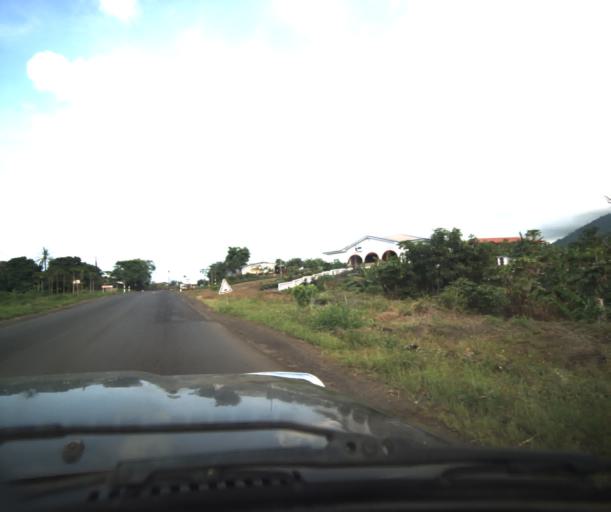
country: CM
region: South-West Province
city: Limbe
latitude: 4.0132
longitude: 9.1551
